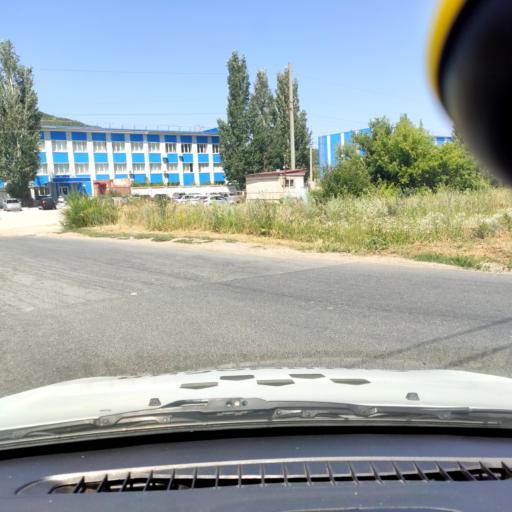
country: RU
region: Samara
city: Zhigulevsk
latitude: 53.4157
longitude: 49.5301
